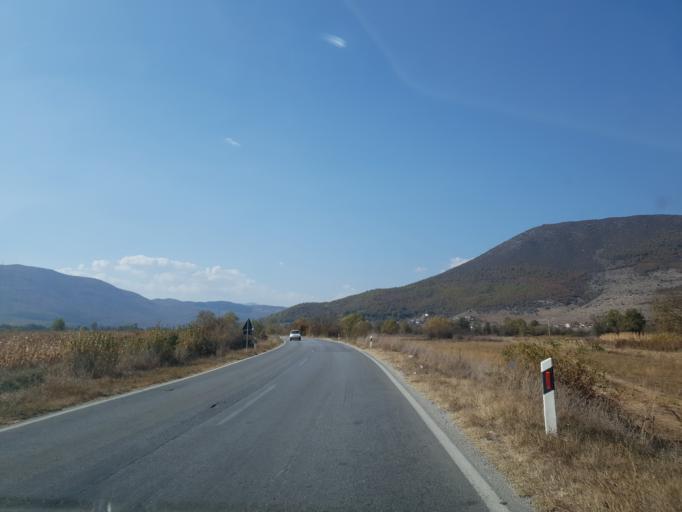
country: MK
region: Plasnica
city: Lisicani
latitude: 41.4702
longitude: 21.0472
